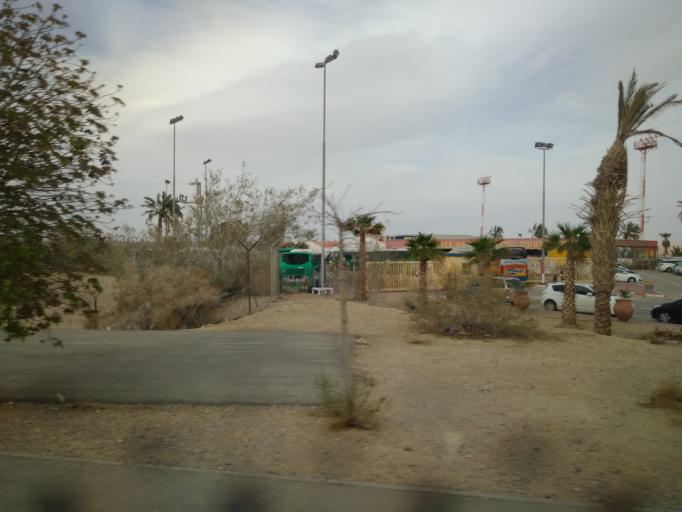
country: IL
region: Southern District
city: Eilat
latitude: 29.9512
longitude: 34.9332
